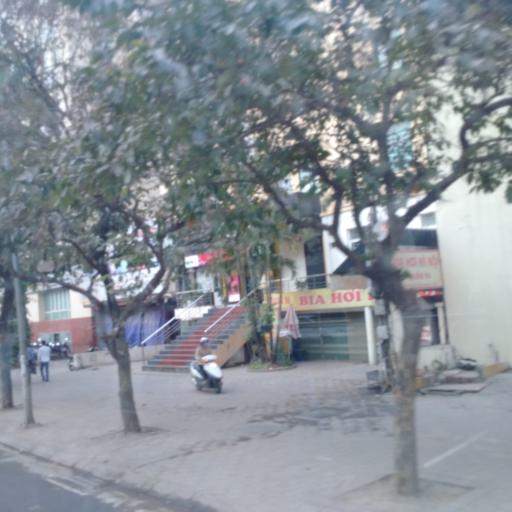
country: VN
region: Ha Noi
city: Cau Giay
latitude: 21.0461
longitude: 105.7969
